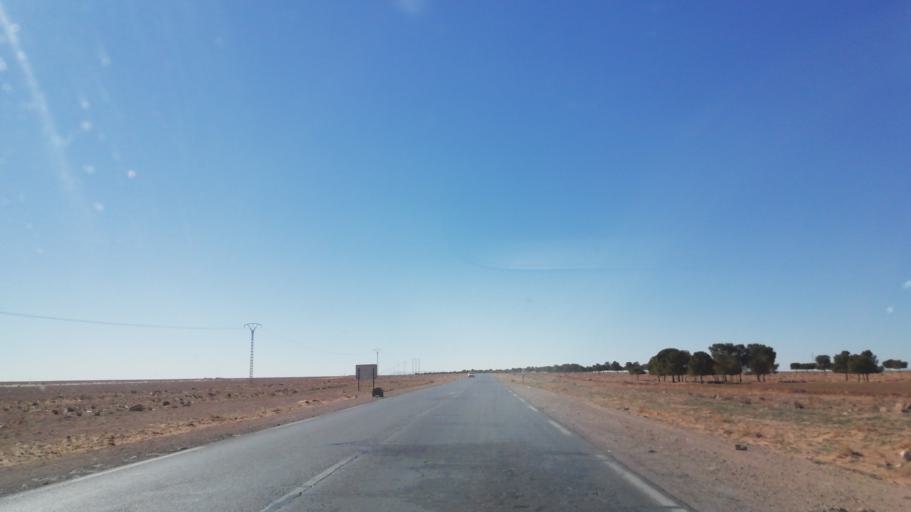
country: DZ
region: Saida
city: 'Ain el Hadjar
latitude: 34.0047
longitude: 0.0472
